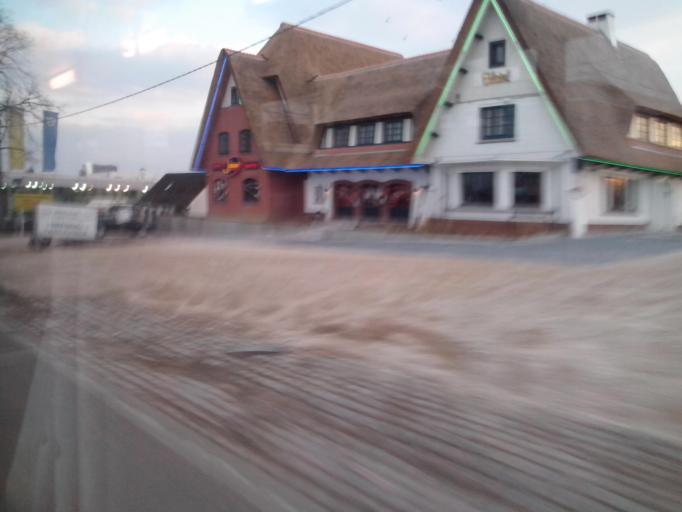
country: BE
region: Flanders
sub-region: Provincie Vlaams-Brabant
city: Asse
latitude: 50.8958
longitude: 4.2388
